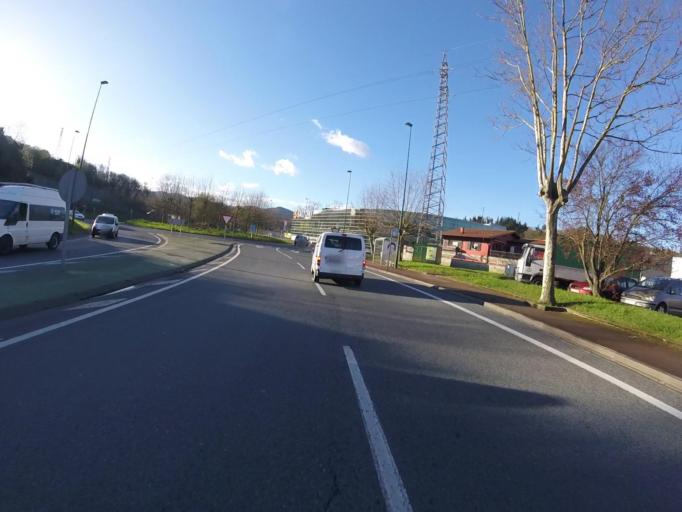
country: ES
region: Basque Country
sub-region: Provincia de Guipuzcoa
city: Errenteria
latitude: 43.3044
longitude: -1.8837
